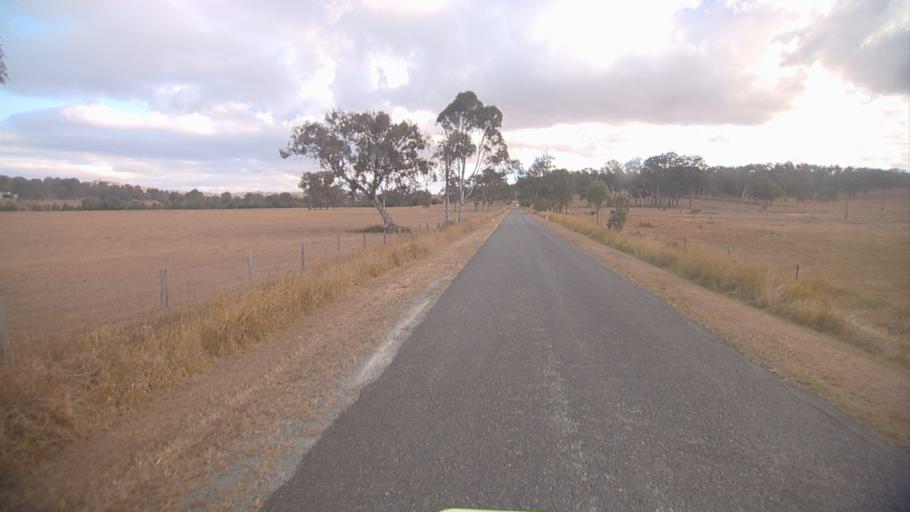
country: AU
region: Queensland
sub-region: Logan
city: Cedar Vale
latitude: -27.8883
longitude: 153.0709
